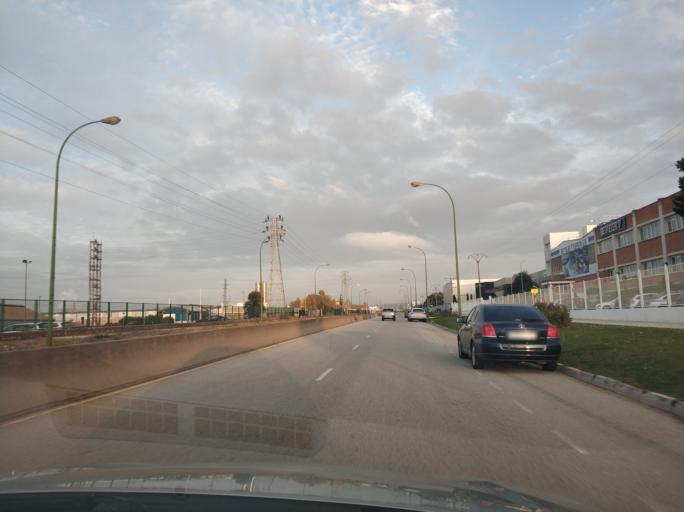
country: ES
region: Castille and Leon
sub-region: Provincia de Burgos
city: Villalbilla de Burgos
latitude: 42.3674
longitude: -3.7489
